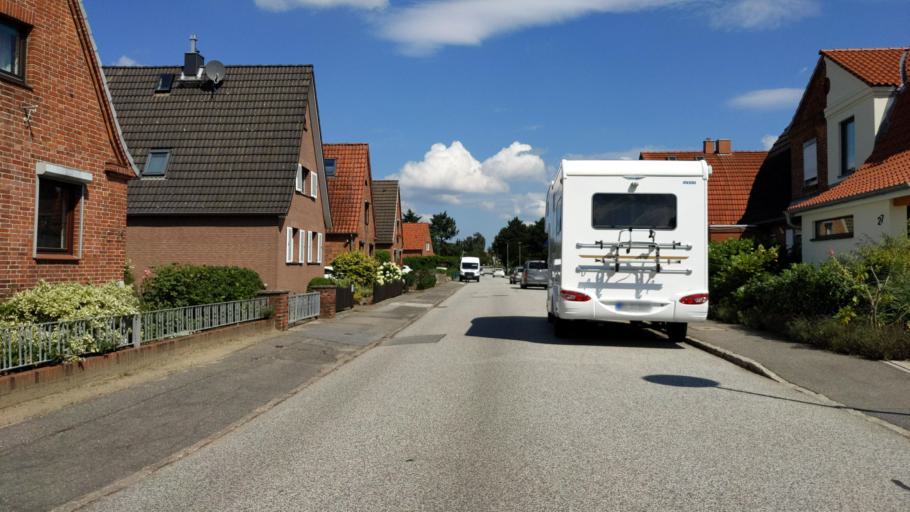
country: DE
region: Schleswig-Holstein
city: Luebeck
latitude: 53.8386
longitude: 10.6787
